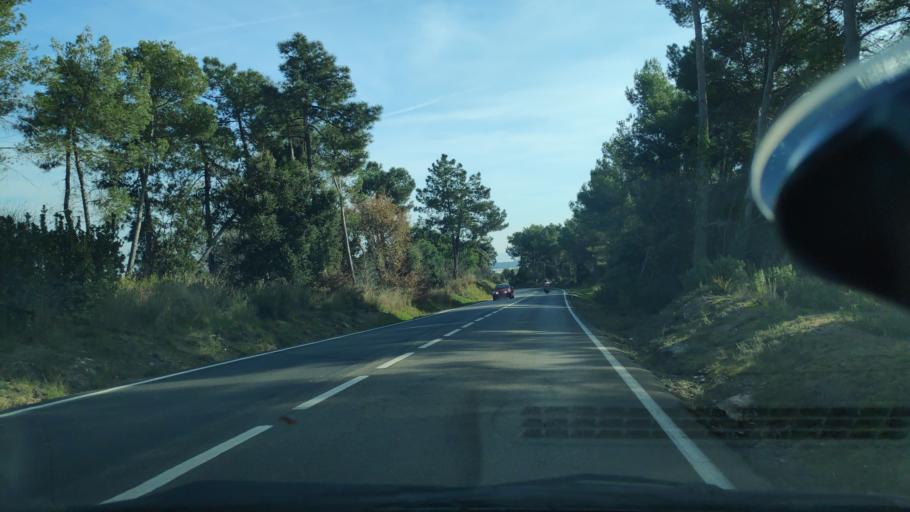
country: ES
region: Catalonia
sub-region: Provincia de Barcelona
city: Castellar del Valles
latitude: 41.6087
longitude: 2.0665
